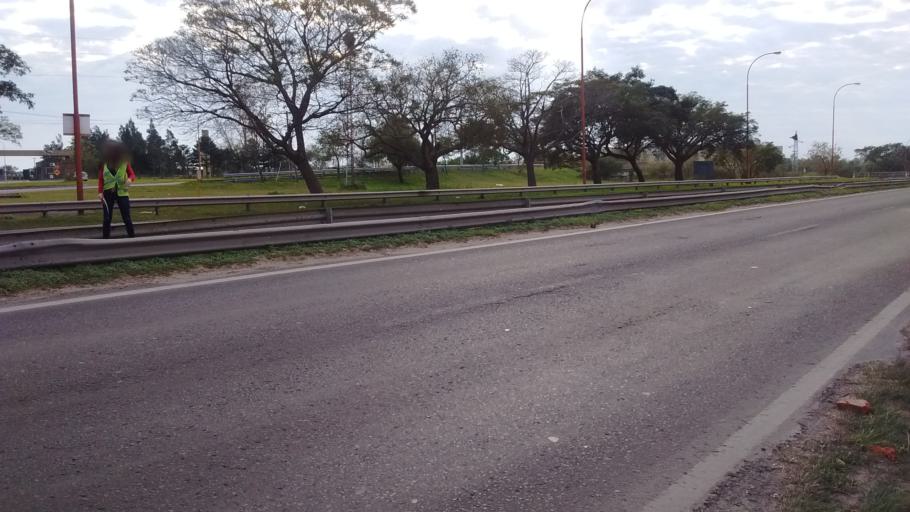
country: AR
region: Santa Fe
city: Santa Fe de la Vera Cruz
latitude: -31.6410
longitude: -60.6669
